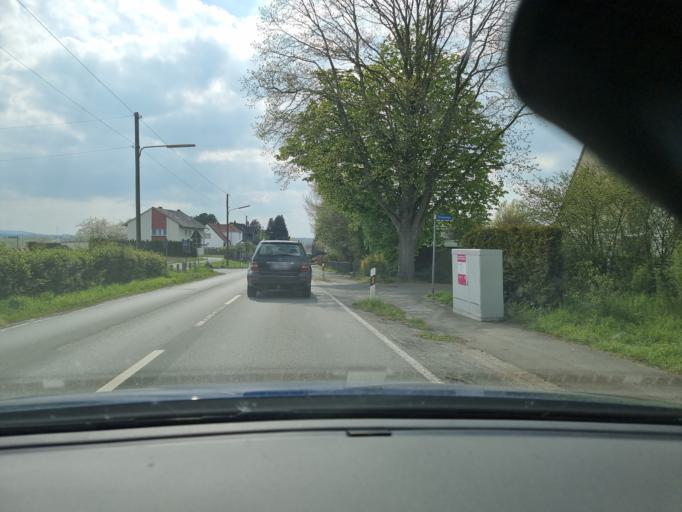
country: DE
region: North Rhine-Westphalia
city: Spenge
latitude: 52.1505
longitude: 8.4943
